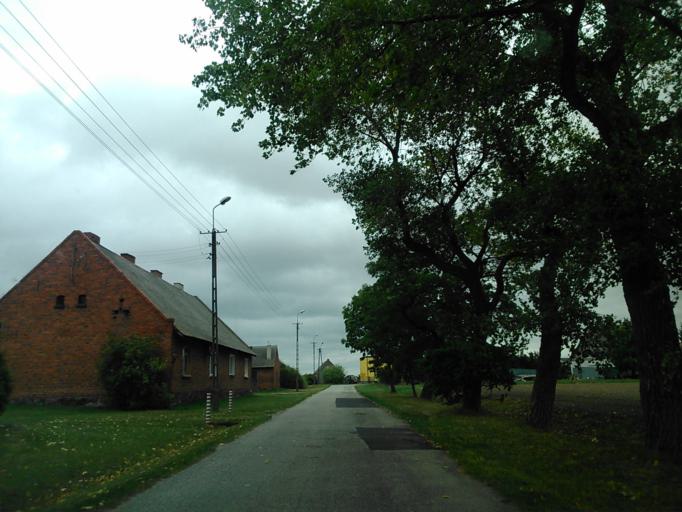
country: PL
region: Greater Poland Voivodeship
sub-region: Powiat koninski
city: Skulsk
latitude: 52.5779
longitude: 18.3777
